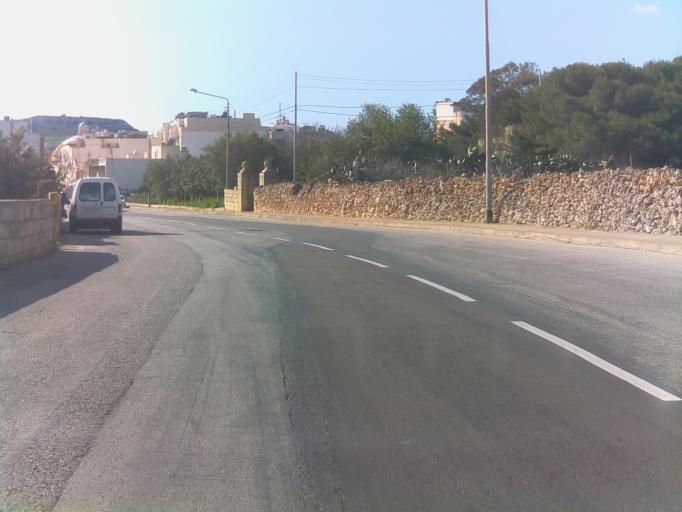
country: MT
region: L-Imgarr
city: Imgarr
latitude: 35.9249
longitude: 14.3675
